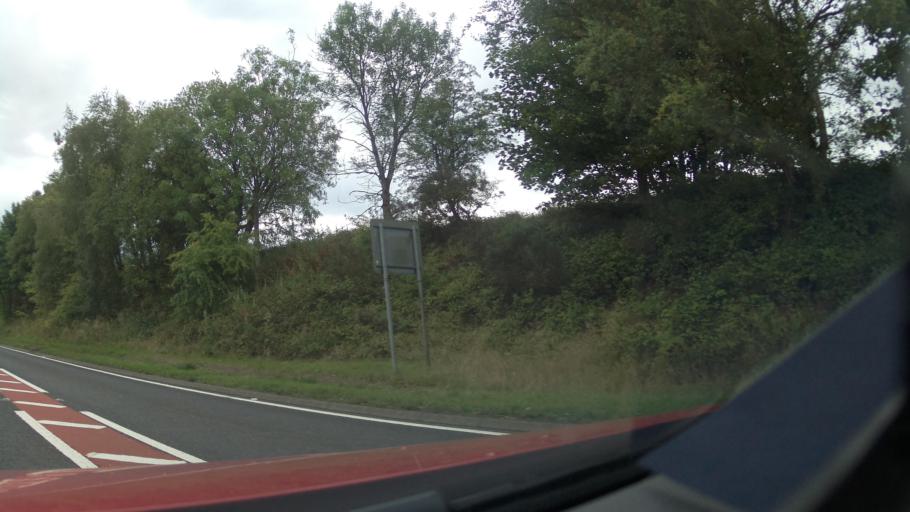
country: GB
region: Scotland
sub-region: Fife
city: High Valleyfield
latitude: 56.0658
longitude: -3.6191
